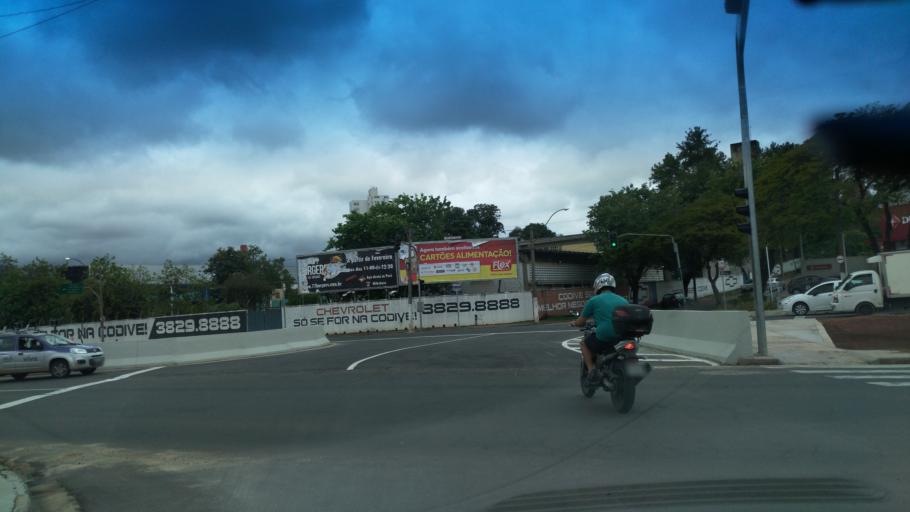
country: BR
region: Sao Paulo
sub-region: Valinhos
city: Valinhos
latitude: -22.9633
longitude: -47.0040
